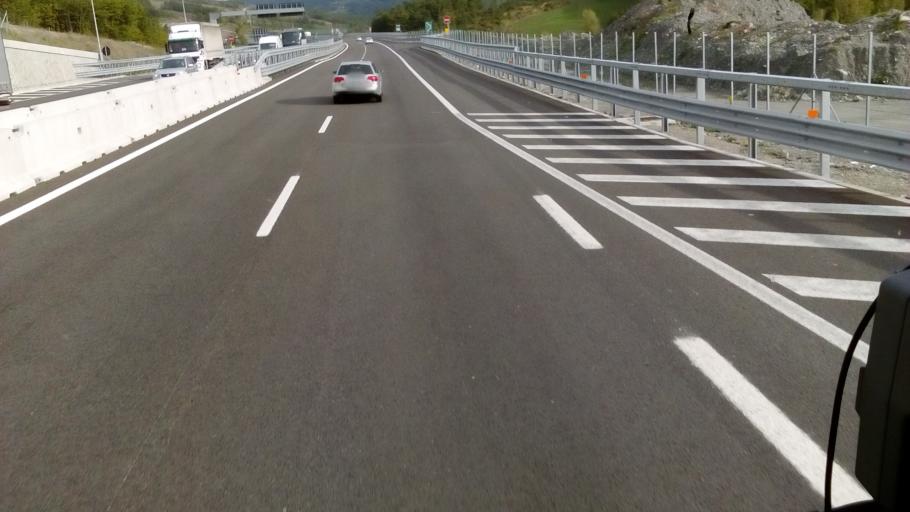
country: IT
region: Emilia-Romagna
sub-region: Provincia di Bologna
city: Castiglione dei Pepoli
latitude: 44.1580
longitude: 11.1964
